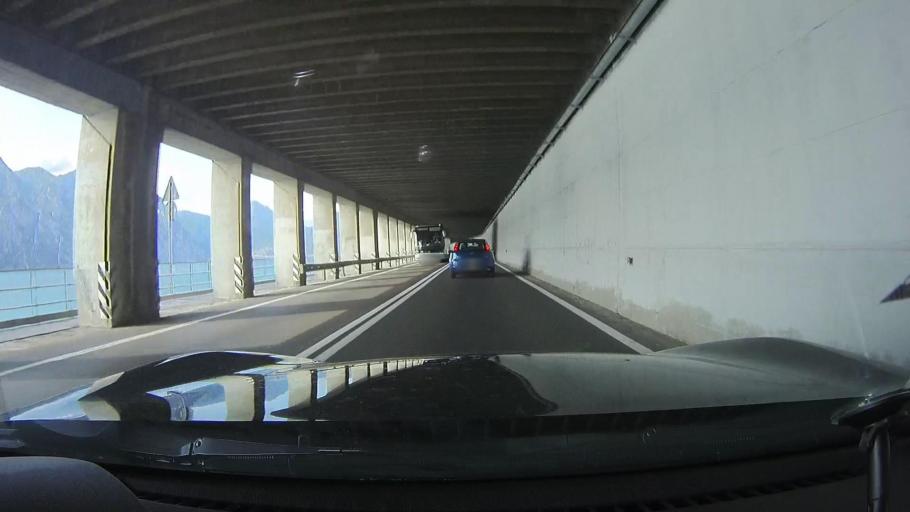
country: IT
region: Trentino-Alto Adige
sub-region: Provincia di Trento
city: Torbole sul Garda
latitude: 45.8198
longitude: 10.8551
